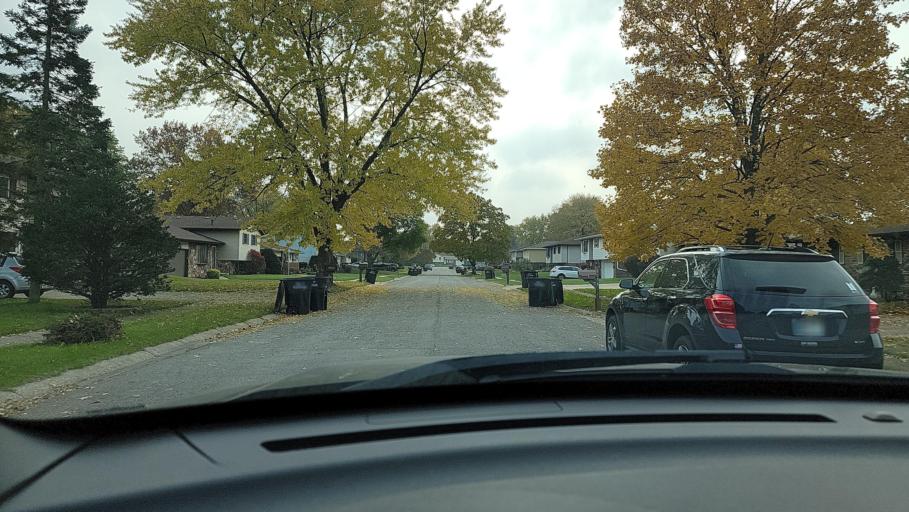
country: US
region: Indiana
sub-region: Porter County
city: Portage
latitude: 41.5926
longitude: -87.1569
